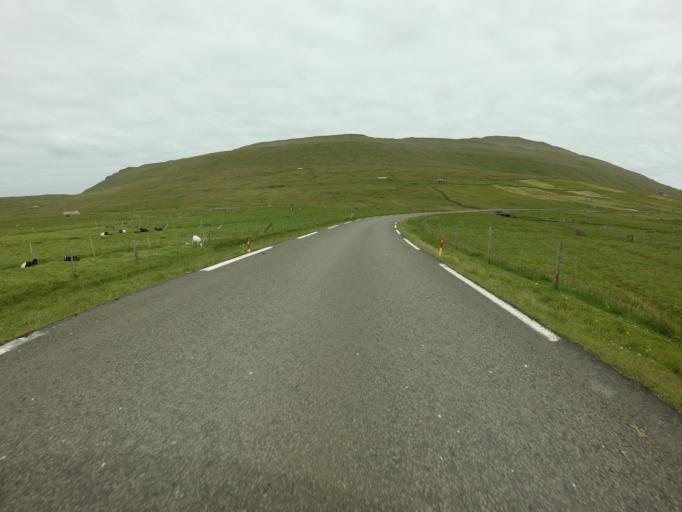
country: FO
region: Suduroy
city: Tvoroyri
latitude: 61.6264
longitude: -6.9434
